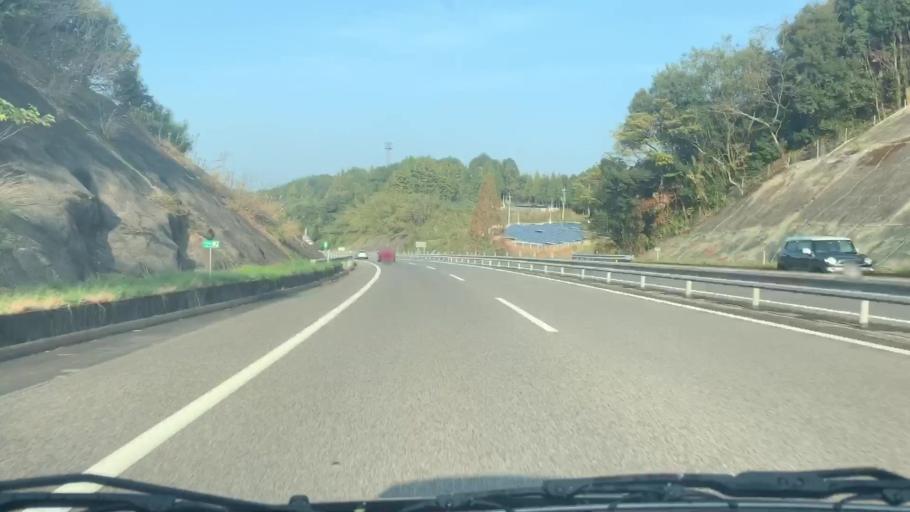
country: JP
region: Saga Prefecture
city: Ureshinomachi-shimojuku
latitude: 33.1533
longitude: 129.9331
